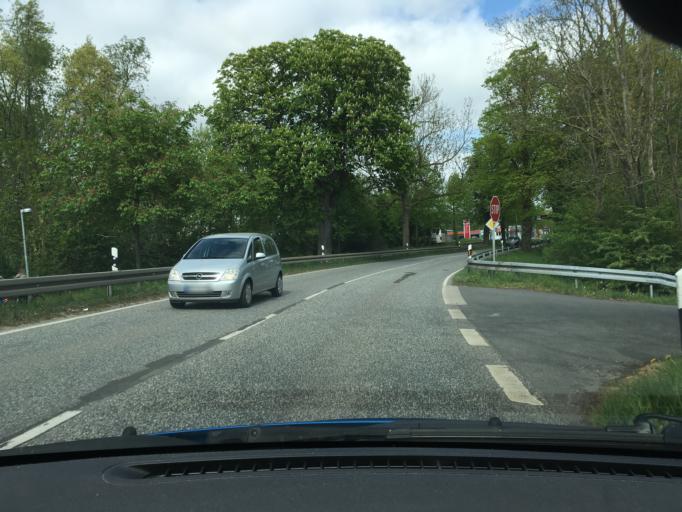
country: DE
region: Mecklenburg-Vorpommern
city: Wismar
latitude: 53.8774
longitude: 11.4516
